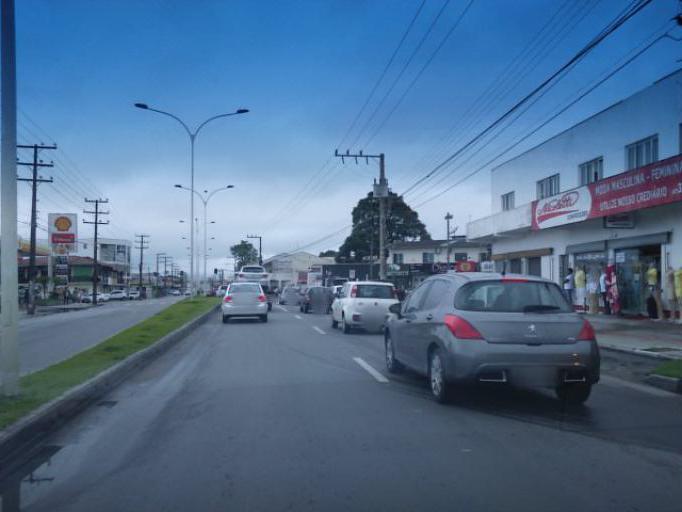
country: BR
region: Santa Catarina
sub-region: Itajai
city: Itajai
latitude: -26.8875
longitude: -48.6994
